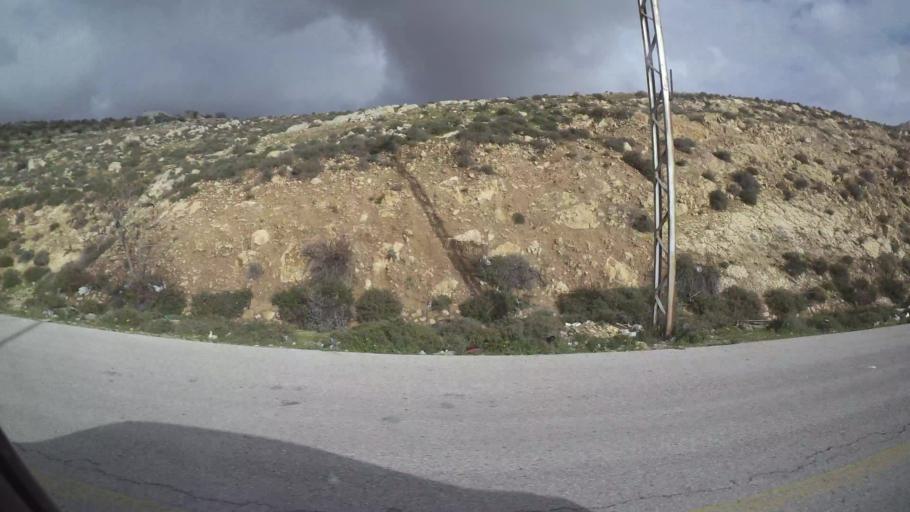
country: JO
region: Amman
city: Al Jubayhah
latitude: 32.0760
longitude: 35.8788
